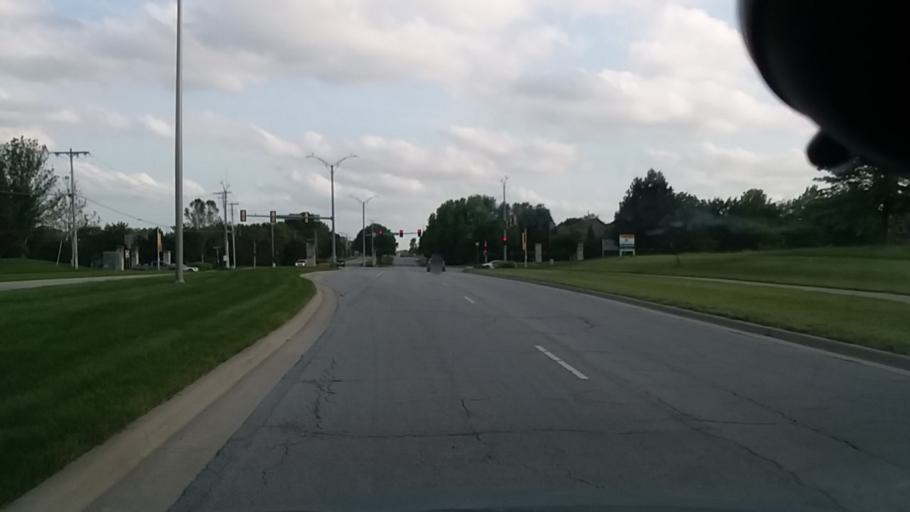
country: US
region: Kansas
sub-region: Johnson County
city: Olathe
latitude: 38.9515
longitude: -94.8162
